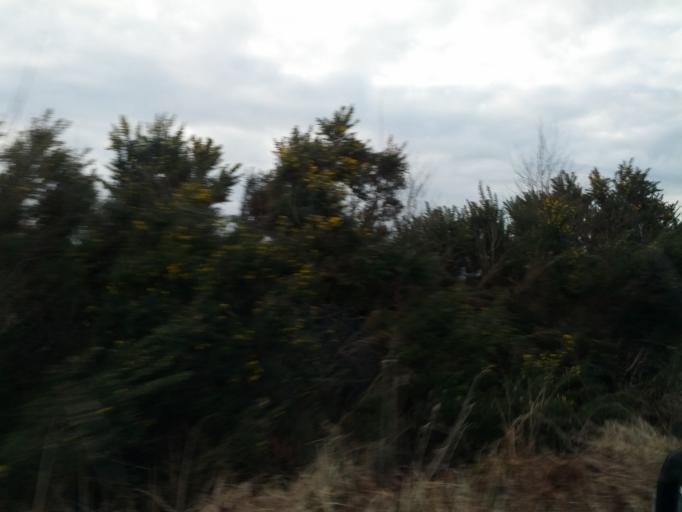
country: IE
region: Connaught
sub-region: County Galway
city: Athenry
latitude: 53.3649
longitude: -8.6653
